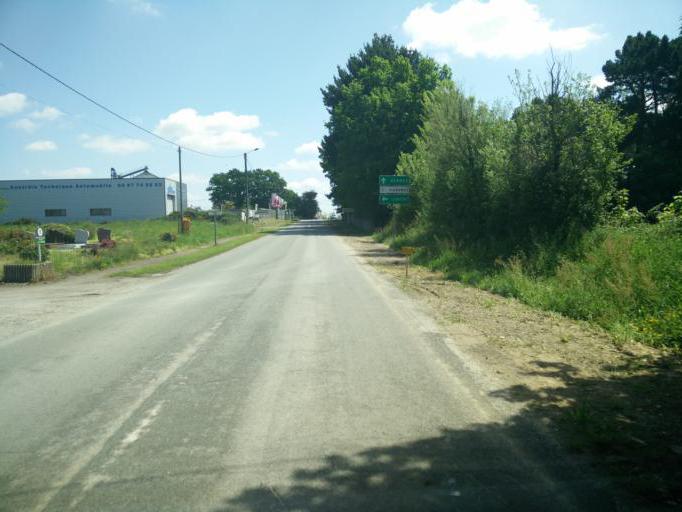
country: FR
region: Brittany
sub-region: Departement du Morbihan
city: Josselin
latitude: 47.9512
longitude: -2.5327
